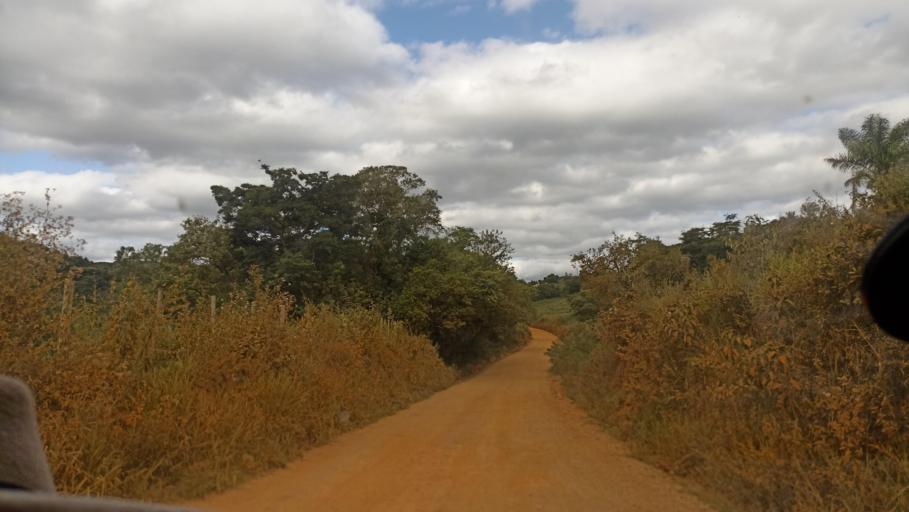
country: BR
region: Minas Gerais
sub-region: Tiradentes
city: Tiradentes
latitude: -21.1020
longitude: -44.1071
